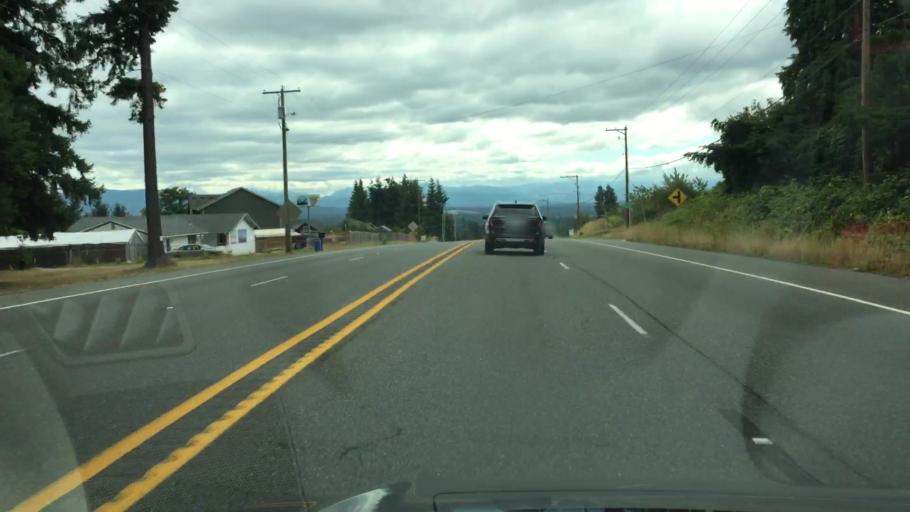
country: US
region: Washington
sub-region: Pierce County
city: Graham
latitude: 47.0281
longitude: -122.2961
